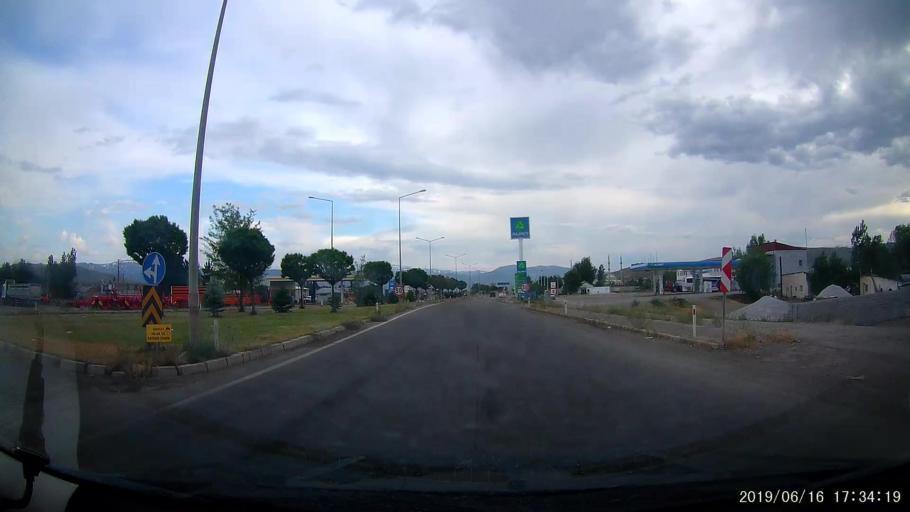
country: TR
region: Erzincan
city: Tercan
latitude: 39.7423
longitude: 40.2696
